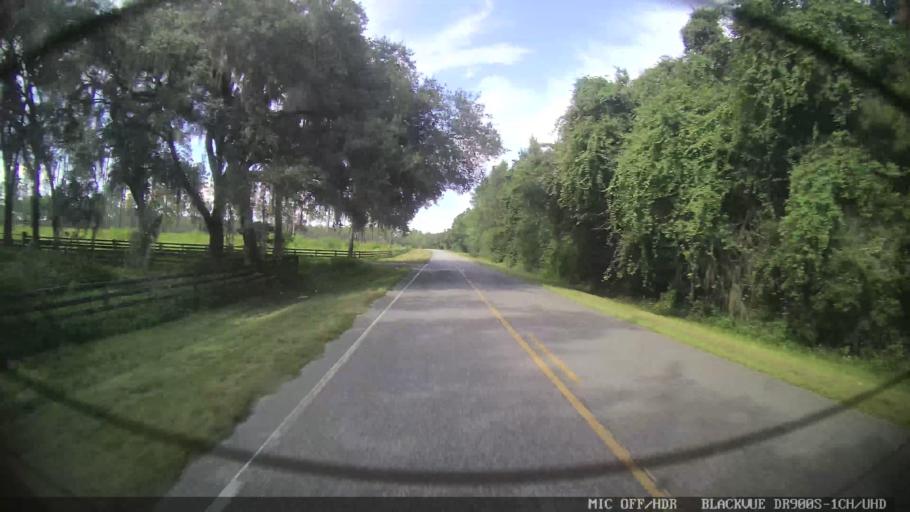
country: US
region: Georgia
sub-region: Echols County
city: Statenville
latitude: 30.6292
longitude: -83.1976
